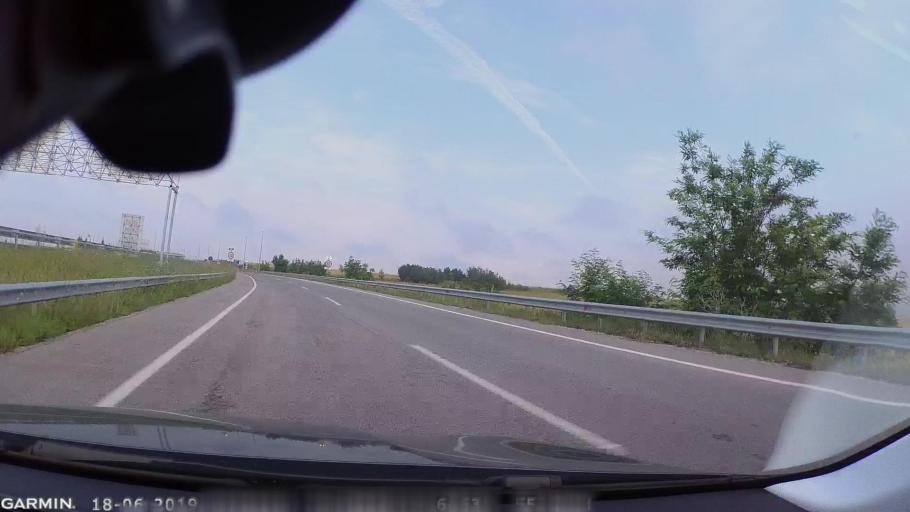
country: MK
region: Petrovec
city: Sredno Konjare
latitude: 41.9544
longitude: 21.7511
